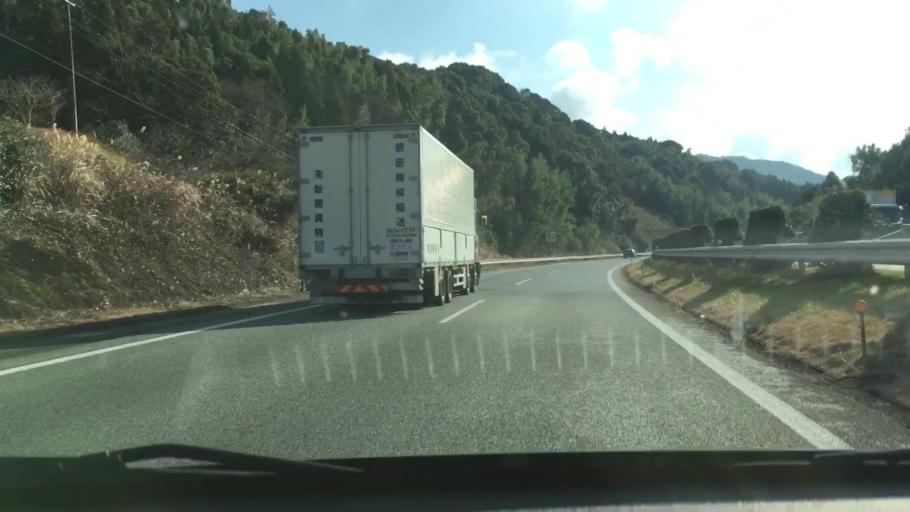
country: JP
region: Kumamoto
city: Matsubase
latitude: 32.6117
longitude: 130.7247
